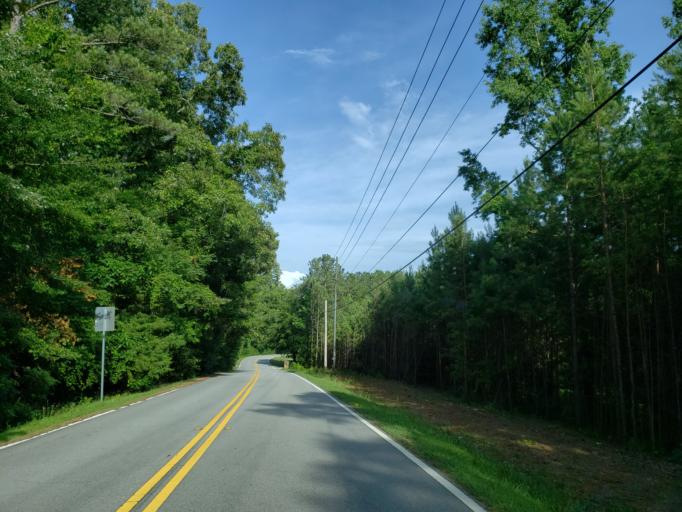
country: US
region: Georgia
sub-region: Paulding County
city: Hiram
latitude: 33.9178
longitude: -84.7209
